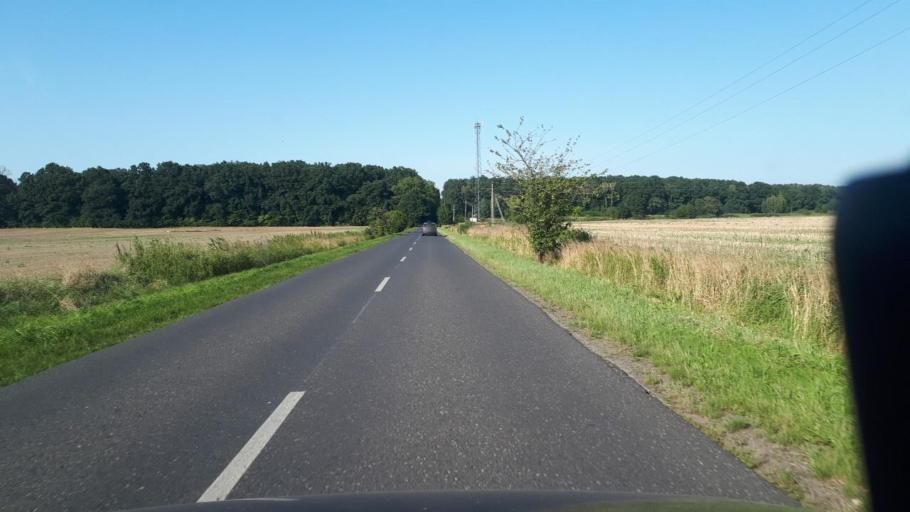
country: PL
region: Silesian Voivodeship
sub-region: Powiat tarnogorski
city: Tworog
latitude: 50.4742
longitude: 18.6817
